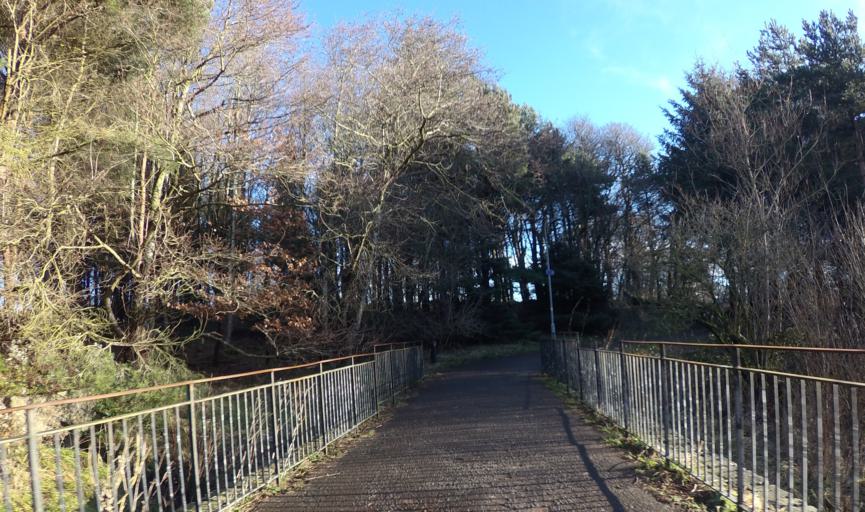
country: GB
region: Scotland
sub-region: West Lothian
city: Mid Calder
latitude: 55.8937
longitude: -3.4914
